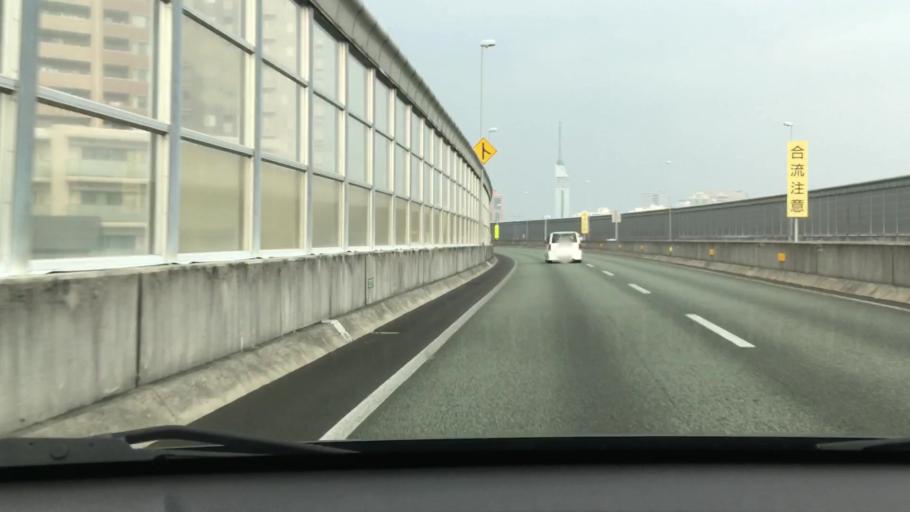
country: JP
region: Fukuoka
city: Fukuoka-shi
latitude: 33.5835
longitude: 130.3391
